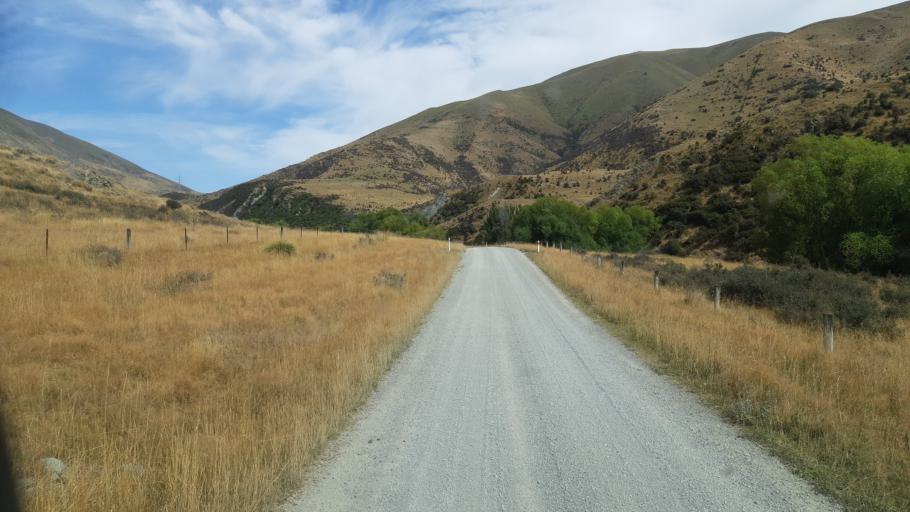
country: NZ
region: Canterbury
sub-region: Timaru District
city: Pleasant Point
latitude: -44.1892
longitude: 170.6559
